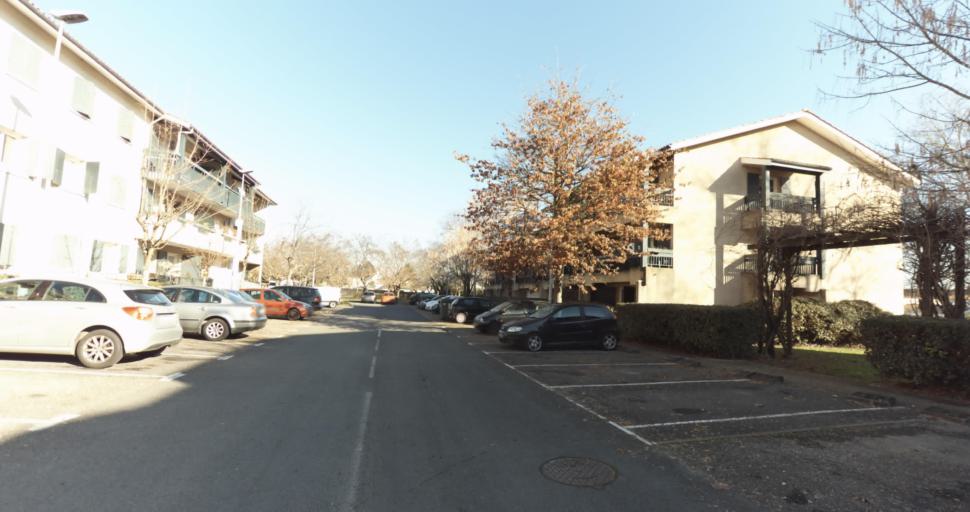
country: FR
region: Aquitaine
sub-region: Departement de la Gironde
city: Carbon-Blanc
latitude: 44.8964
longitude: -0.5008
